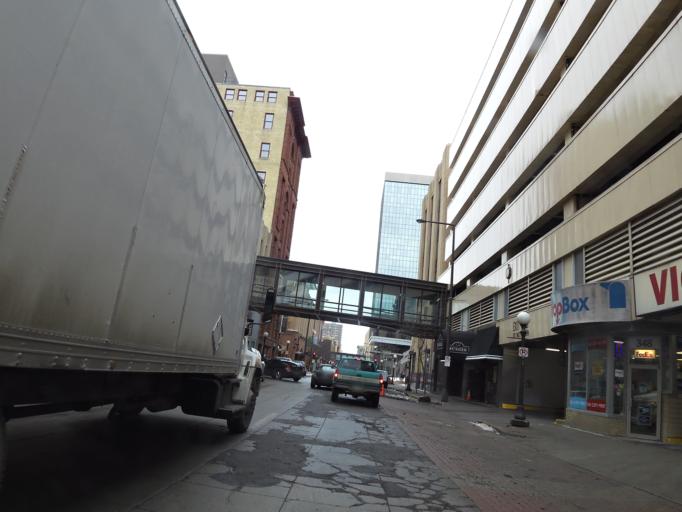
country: US
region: Minnesota
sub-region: Ramsey County
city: Saint Paul
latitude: 44.9451
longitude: -93.0939
